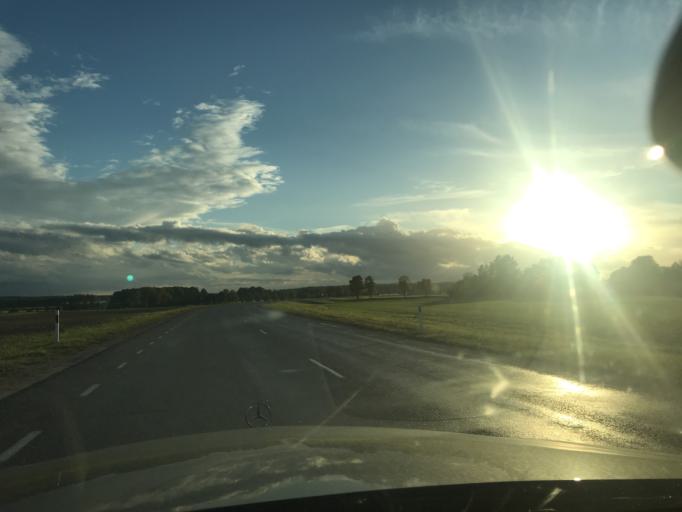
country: EE
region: Vorumaa
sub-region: Voru linn
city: Voru
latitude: 57.8673
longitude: 26.9253
